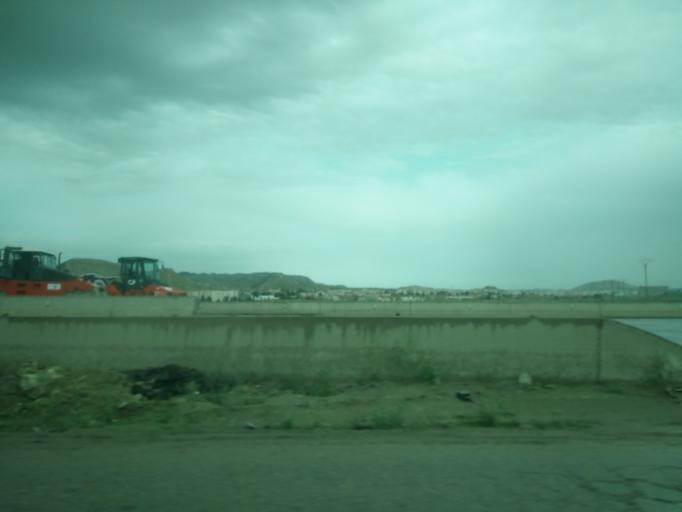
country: DZ
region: Medea
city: Ksar el Boukhari
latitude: 35.8801
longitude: 2.7350
